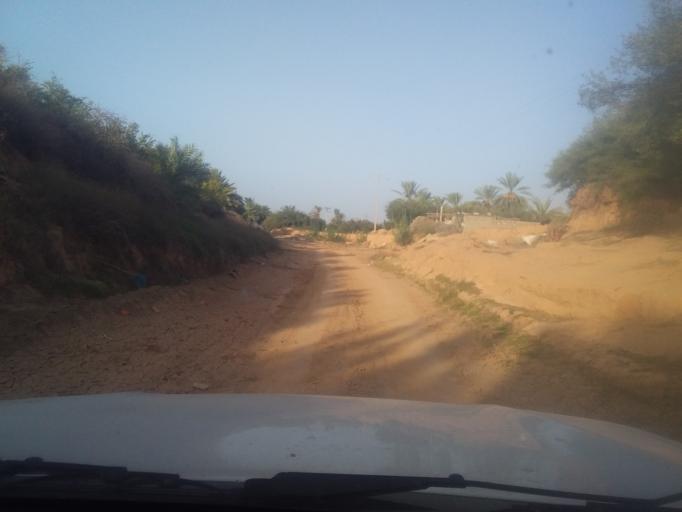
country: TN
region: Qabis
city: Gabes
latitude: 33.6305
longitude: 10.3009
